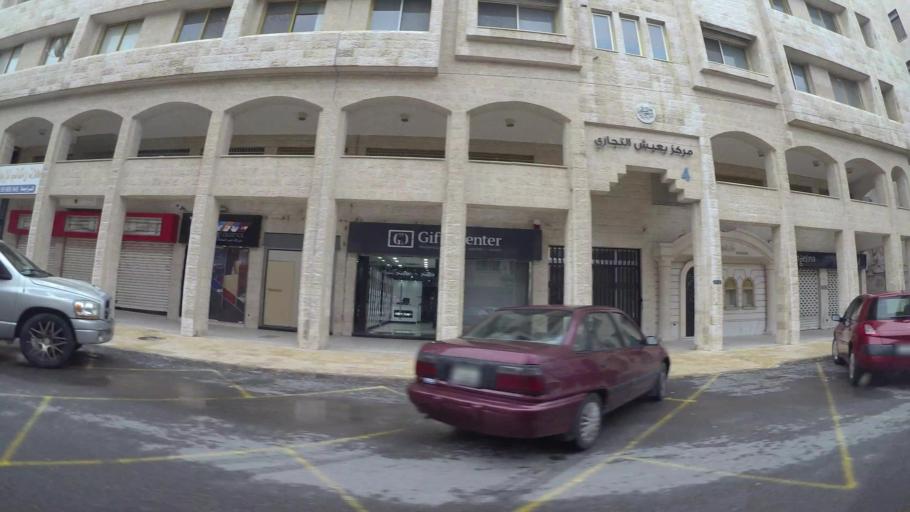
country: JO
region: Amman
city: Wadi as Sir
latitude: 31.9572
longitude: 35.8683
